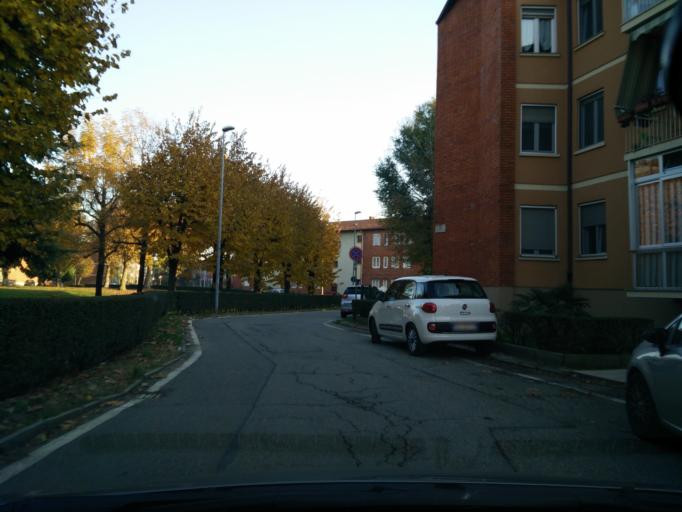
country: IT
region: Piedmont
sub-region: Provincia di Torino
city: Leini
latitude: 45.1284
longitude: 7.7072
